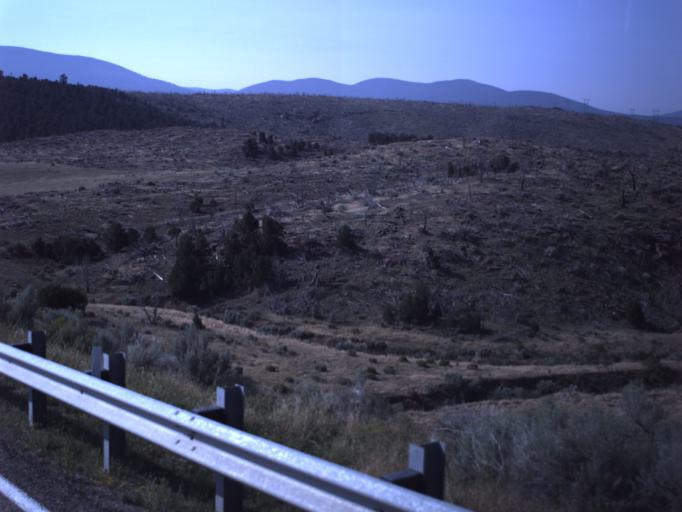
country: US
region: Utah
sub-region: Daggett County
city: Manila
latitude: 40.9374
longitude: -109.4070
